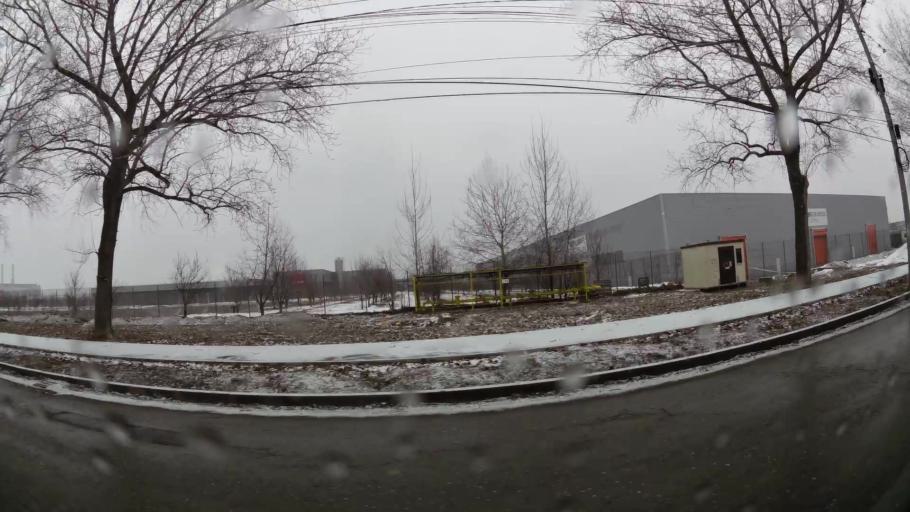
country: RO
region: Dambovita
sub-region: Municipiul Targoviste
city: Targoviste
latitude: 44.9191
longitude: 25.4368
